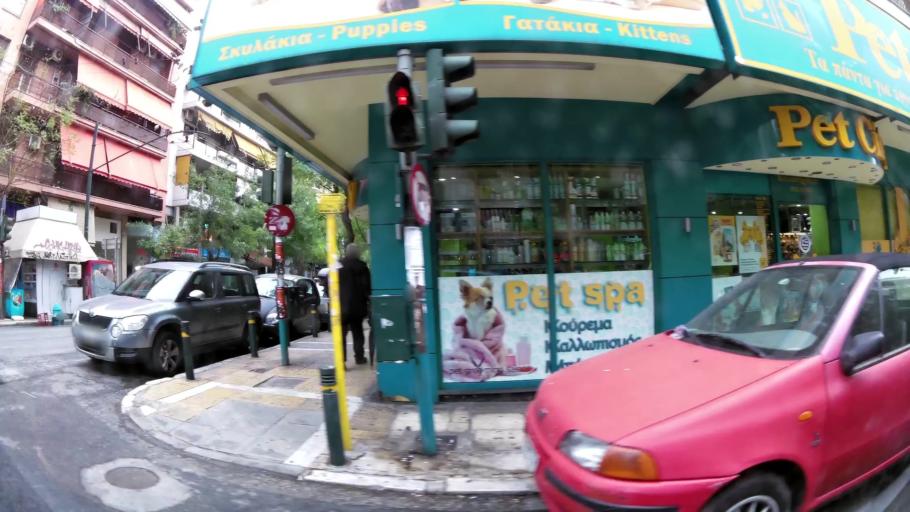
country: GR
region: Attica
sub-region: Nomarchia Athinas
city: Vyronas
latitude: 37.9678
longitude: 23.7541
